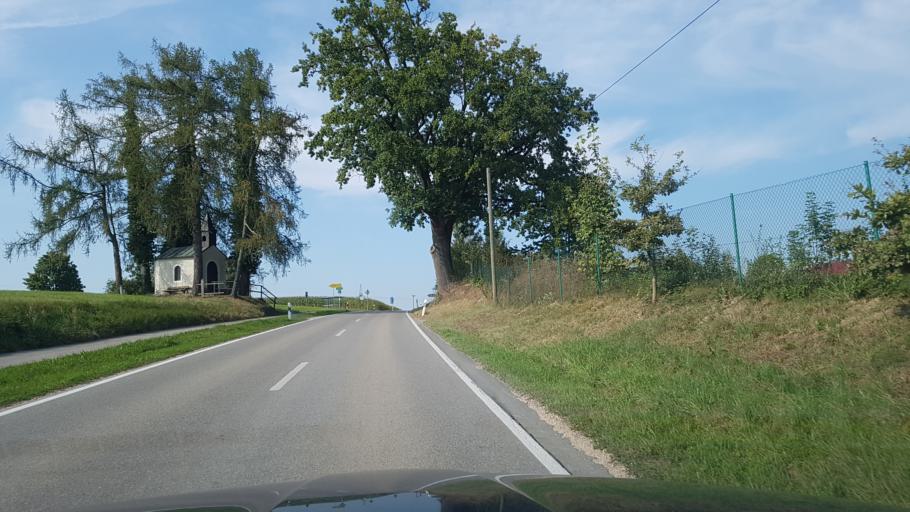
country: DE
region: Bavaria
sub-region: Upper Bavaria
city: Laufen
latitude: 47.8817
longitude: 12.9258
